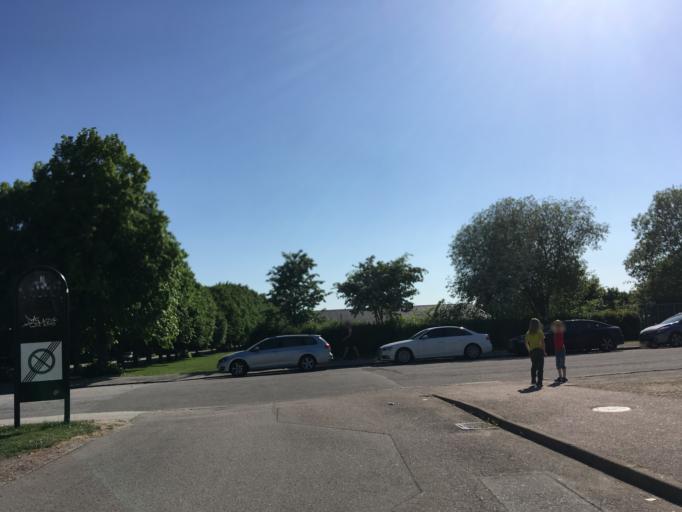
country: SE
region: Skane
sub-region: Lunds Kommun
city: Lund
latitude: 55.6951
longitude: 13.1759
